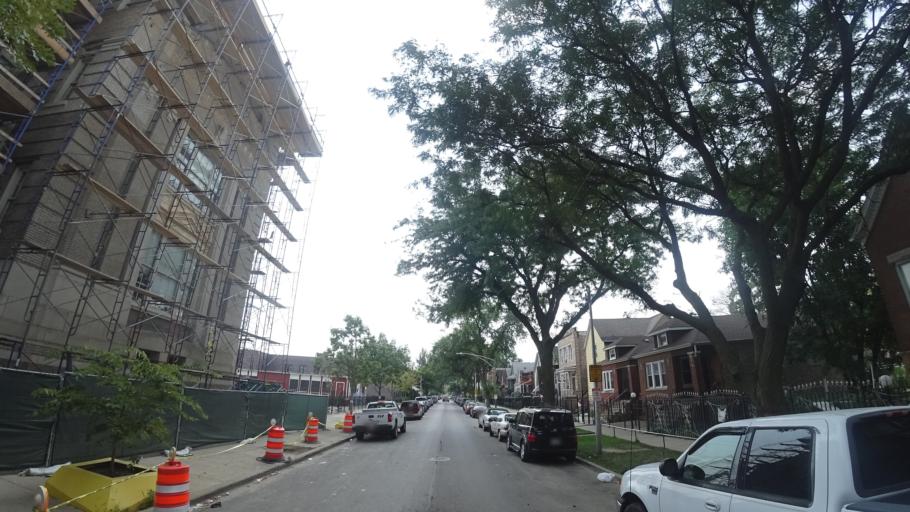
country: US
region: Illinois
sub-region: Cook County
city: Cicero
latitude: 41.8400
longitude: -87.7257
